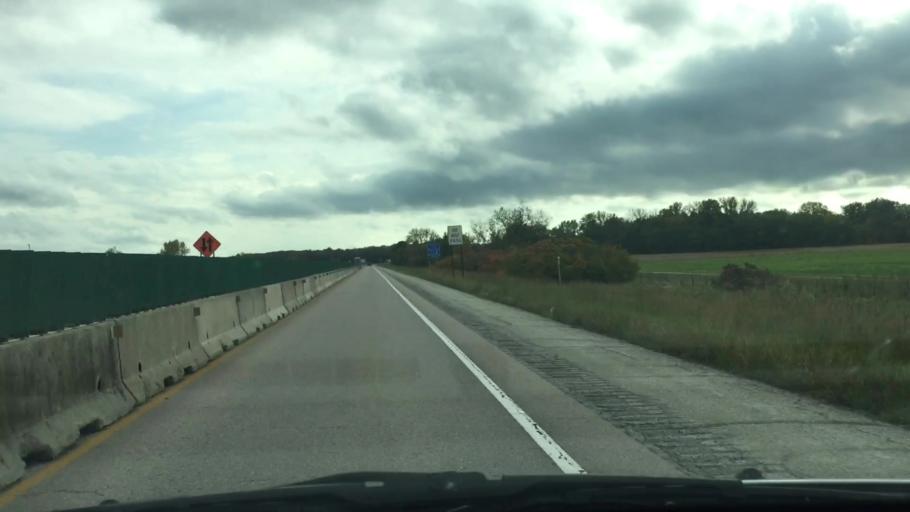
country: US
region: Iowa
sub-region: Decatur County
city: Lamoni
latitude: 40.6735
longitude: -93.8502
